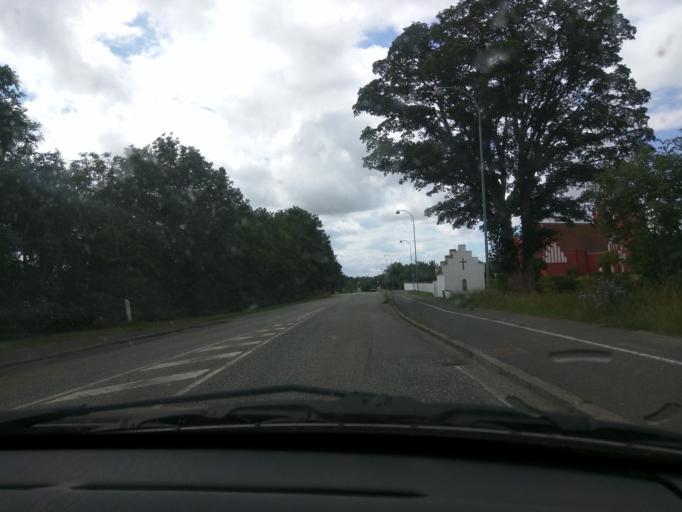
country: DK
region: Zealand
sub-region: Kalundborg Kommune
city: Svebolle
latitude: 55.6847
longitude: 11.3119
